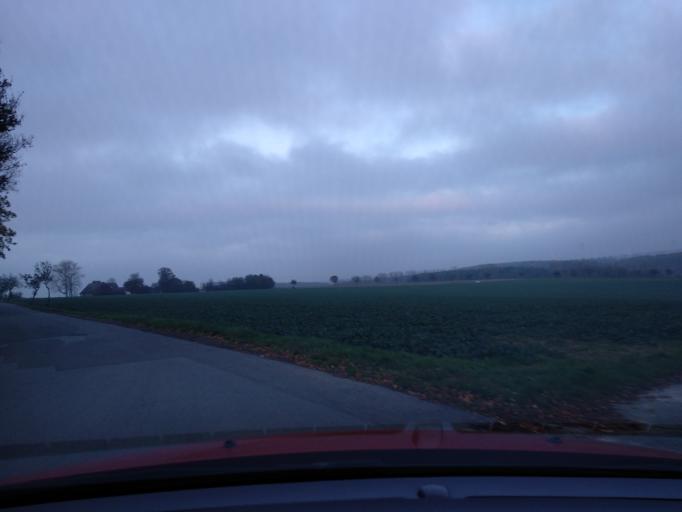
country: DE
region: North Rhine-Westphalia
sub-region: Regierungsbezirk Detmold
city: Paderborn
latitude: 51.6759
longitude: 8.7691
